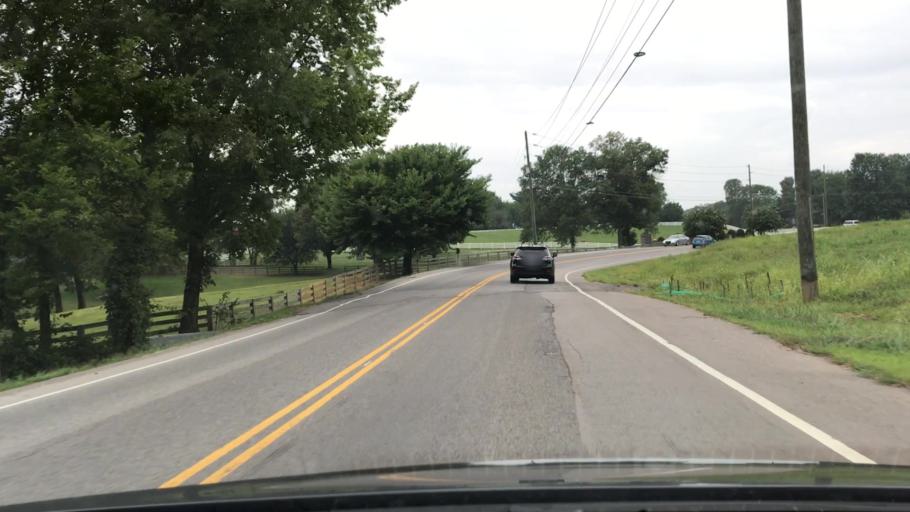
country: US
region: Tennessee
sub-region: Williamson County
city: Nolensville
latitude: 35.9280
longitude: -86.7458
